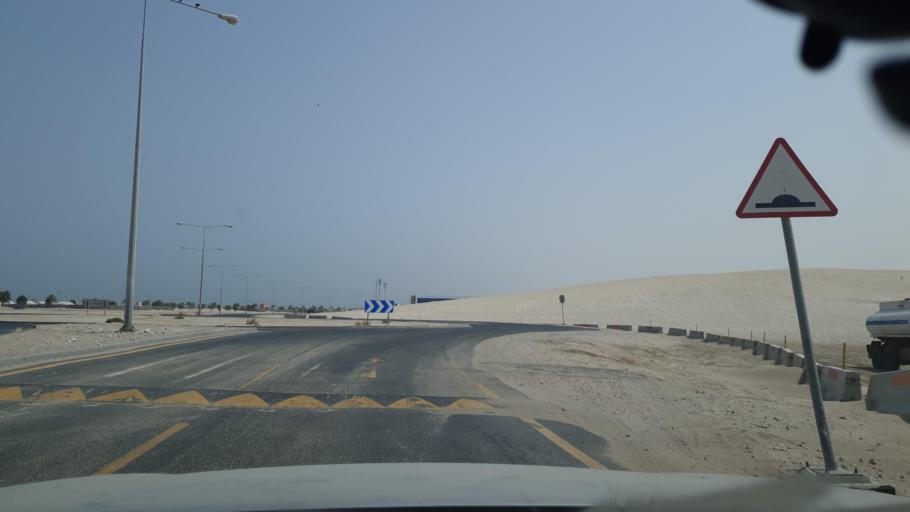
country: QA
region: Al Wakrah
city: Umm Sa'id
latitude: 24.8592
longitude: 51.5107
